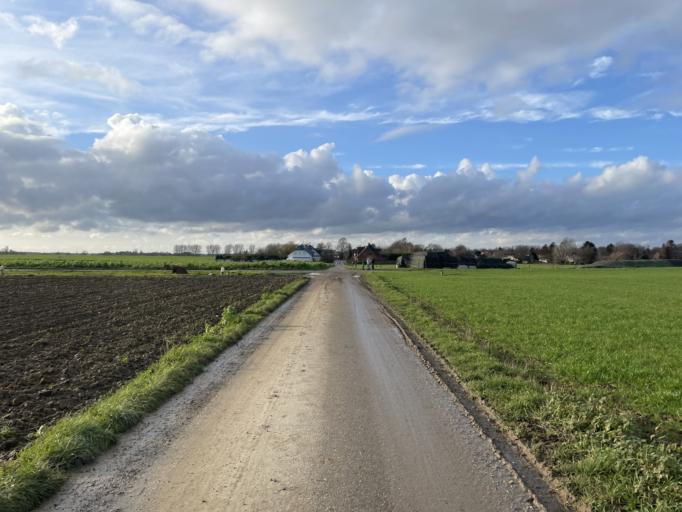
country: DE
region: North Rhine-Westphalia
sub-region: Regierungsbezirk Koln
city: Titz
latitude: 51.0785
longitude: 6.4186
